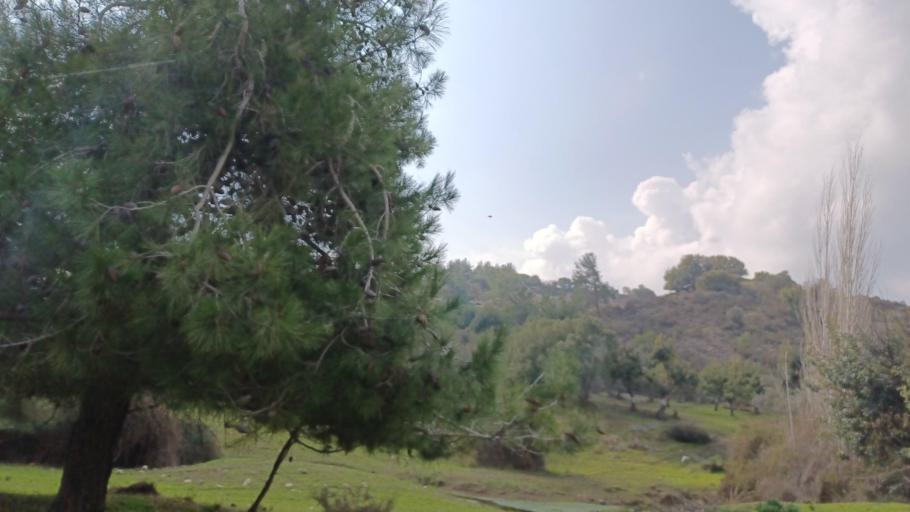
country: CY
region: Pafos
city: Polis
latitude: 34.9948
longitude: 32.5351
